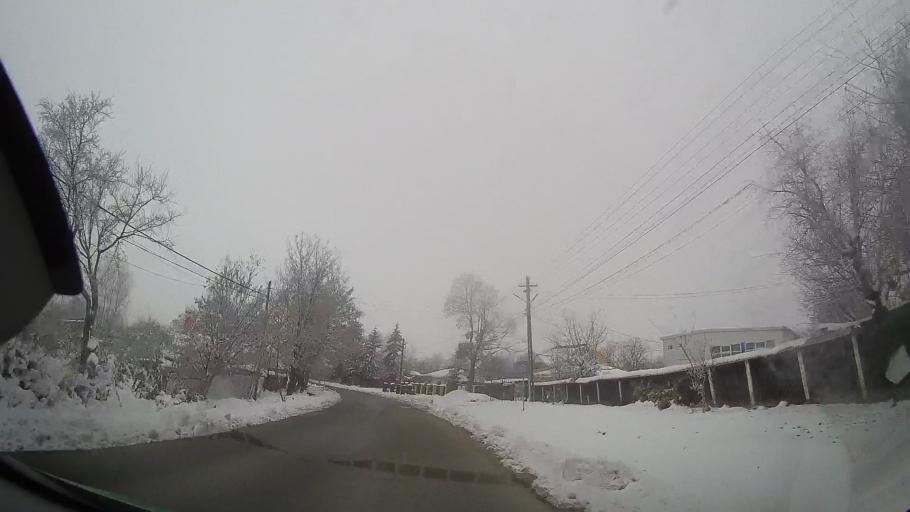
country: RO
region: Neamt
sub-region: Comuna Icusesti
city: Balusesti
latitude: 46.8607
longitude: 27.0188
